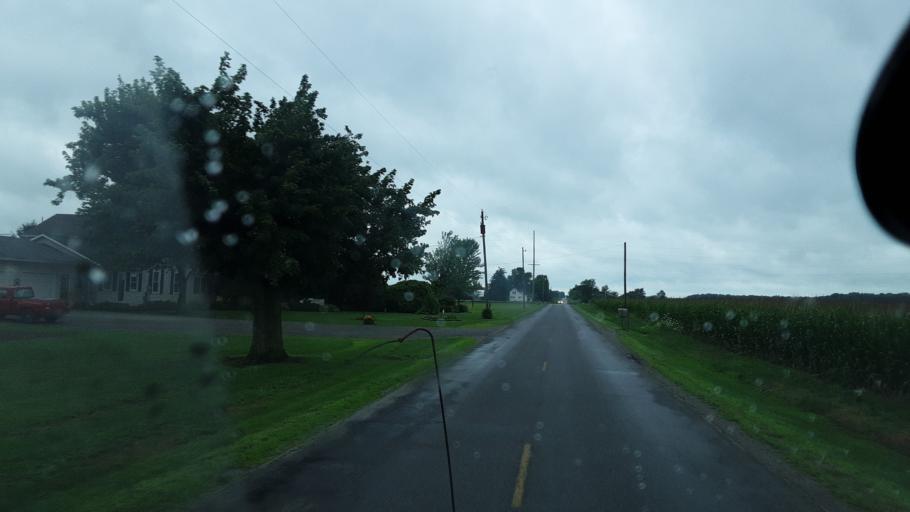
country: US
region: Ohio
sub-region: Van Wert County
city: Van Wert
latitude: 40.8003
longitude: -84.6455
